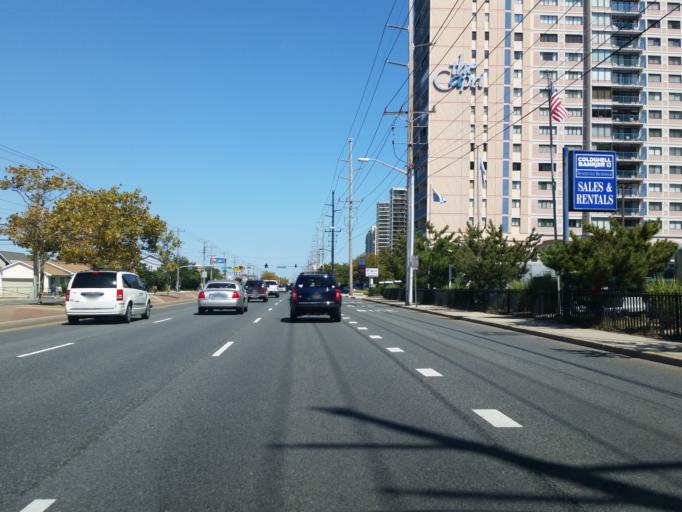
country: US
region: Maryland
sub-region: Worcester County
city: Ocean City
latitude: 38.4164
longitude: -75.0573
